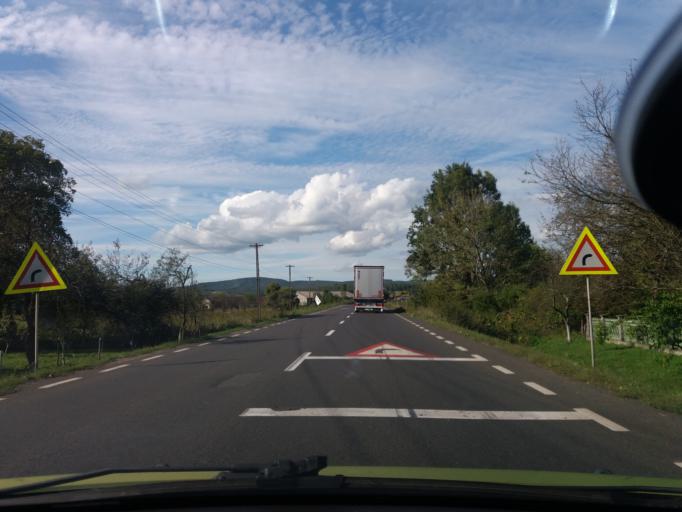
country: RO
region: Arad
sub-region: Comuna Varadia de Mures
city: Varadia de Mures
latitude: 46.0110
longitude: 22.1495
